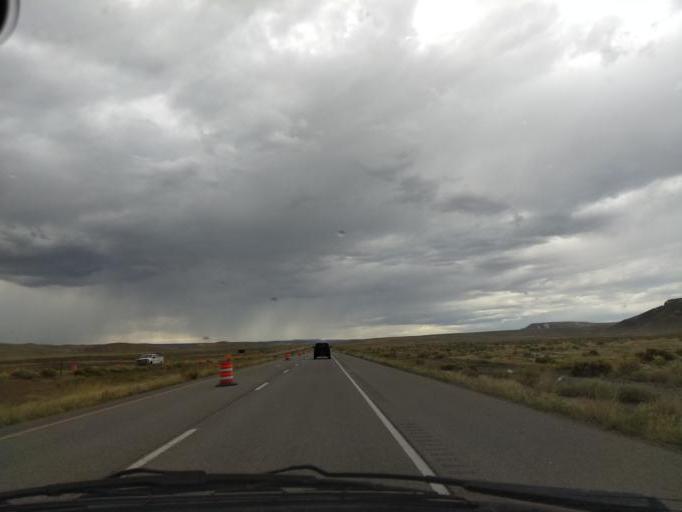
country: US
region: Colorado
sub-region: Delta County
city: Delta
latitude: 38.7622
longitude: -108.1996
